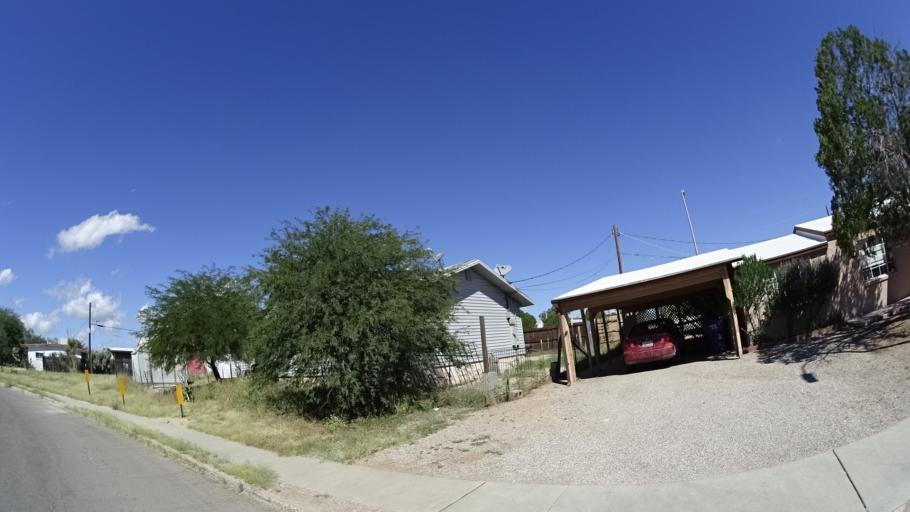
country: US
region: Arizona
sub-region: Pima County
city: Tucson
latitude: 32.2468
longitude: -110.9647
